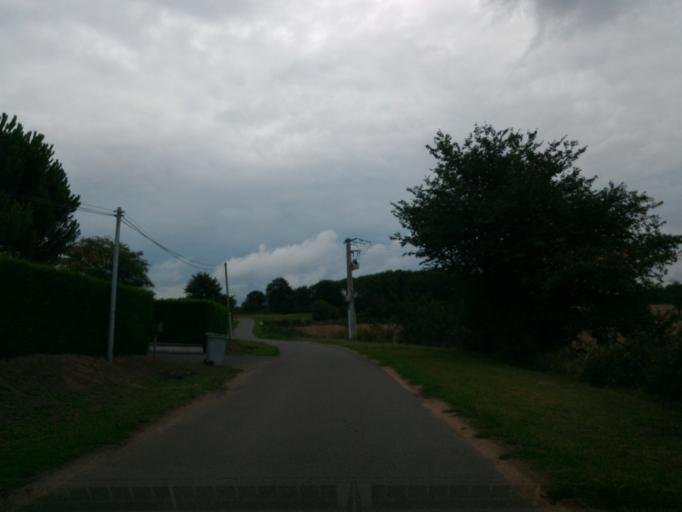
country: FR
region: Poitou-Charentes
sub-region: Departement de la Charente
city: Etagnac
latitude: 45.9054
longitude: 0.7533
